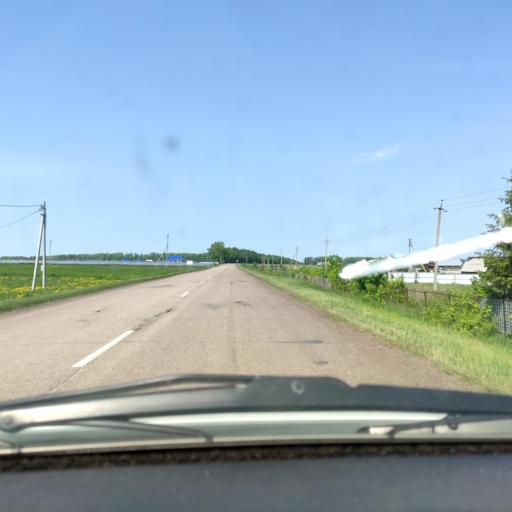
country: RU
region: Bashkortostan
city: Avdon
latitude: 54.5013
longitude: 55.6188
